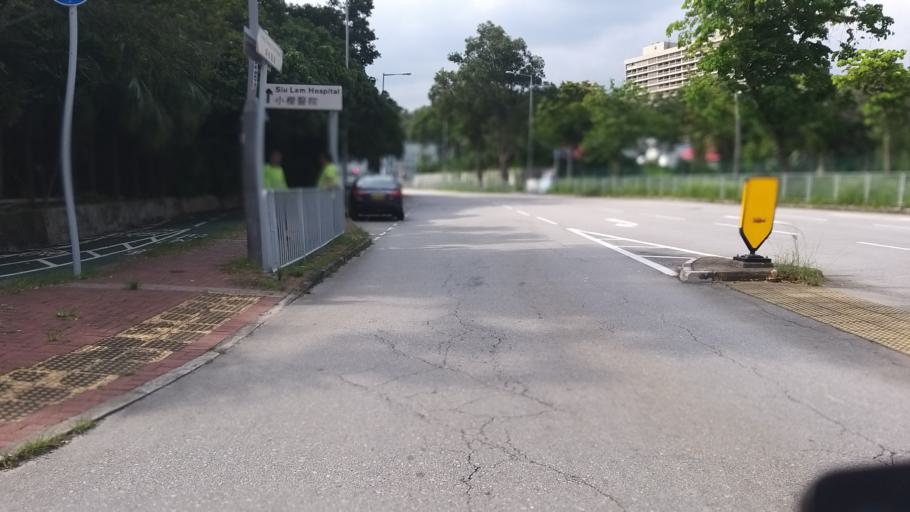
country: HK
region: Tuen Mun
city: Tuen Mun
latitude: 22.4067
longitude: 113.9748
